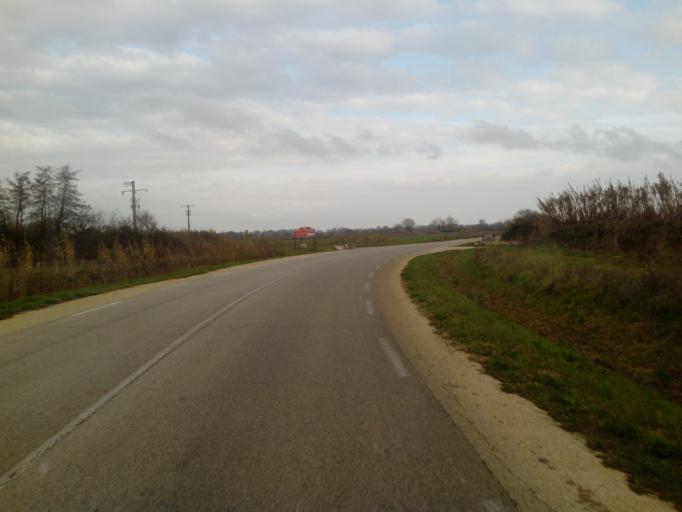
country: FR
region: Provence-Alpes-Cote d'Azur
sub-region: Departement des Bouches-du-Rhone
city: Saintes-Maries-de-la-Mer
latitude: 43.5502
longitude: 4.3805
